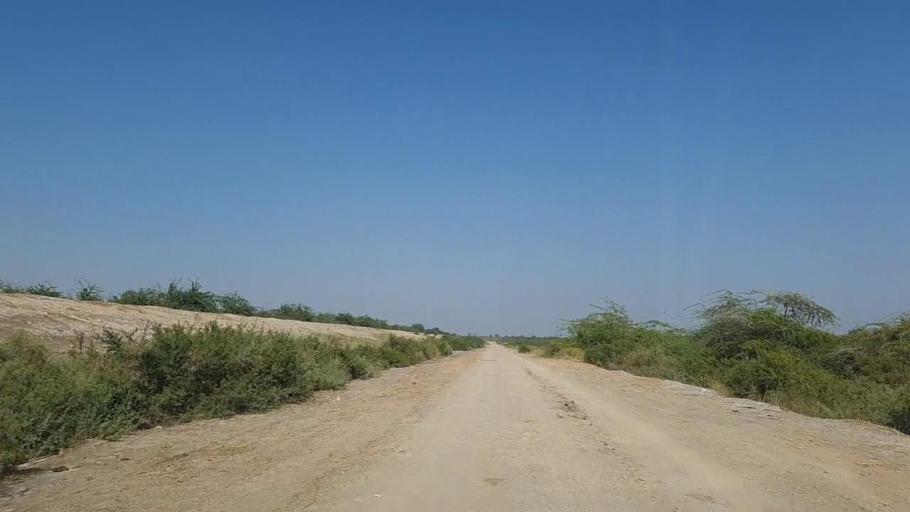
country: PK
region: Sindh
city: Thatta
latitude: 24.5878
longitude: 68.0400
